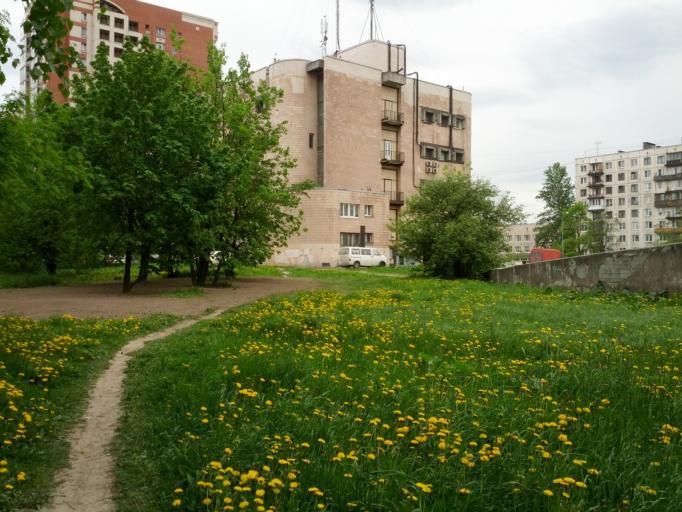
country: RU
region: St.-Petersburg
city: Obukhovo
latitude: 59.8966
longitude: 30.4777
